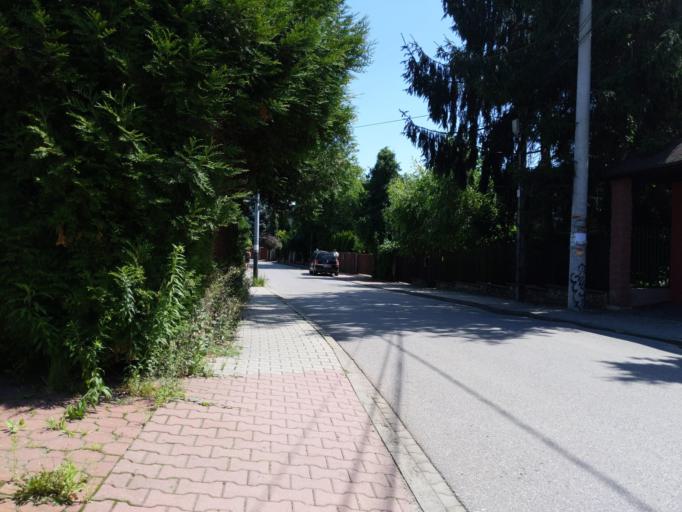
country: PL
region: Lesser Poland Voivodeship
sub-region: Krakow
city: Krakow
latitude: 50.0360
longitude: 19.9917
